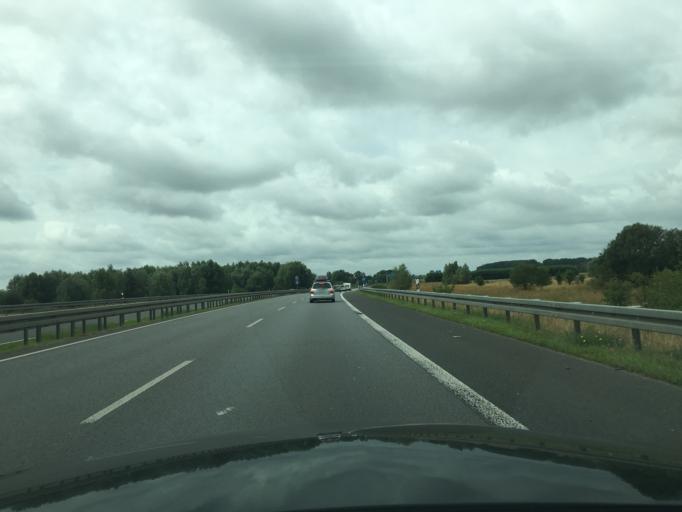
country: DE
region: Brandenburg
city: Leegebruch
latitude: 52.7119
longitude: 13.2138
